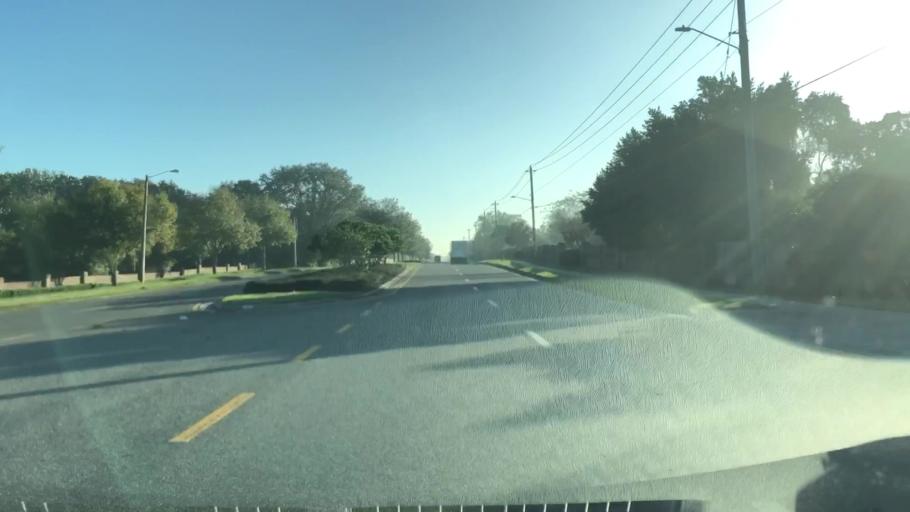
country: US
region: Florida
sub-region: Seminole County
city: Lake Mary
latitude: 28.7864
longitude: -81.3363
